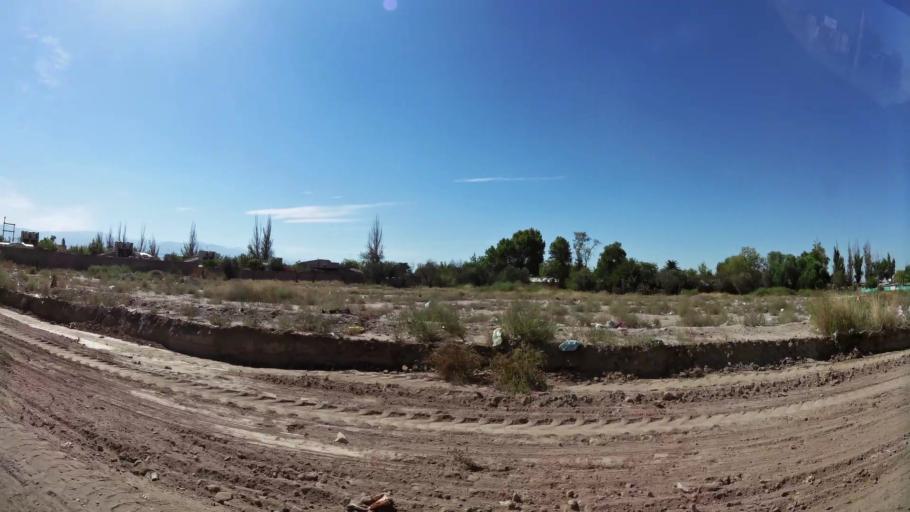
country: AR
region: Mendoza
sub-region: Departamento de Godoy Cruz
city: Godoy Cruz
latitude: -32.9553
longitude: -68.8245
